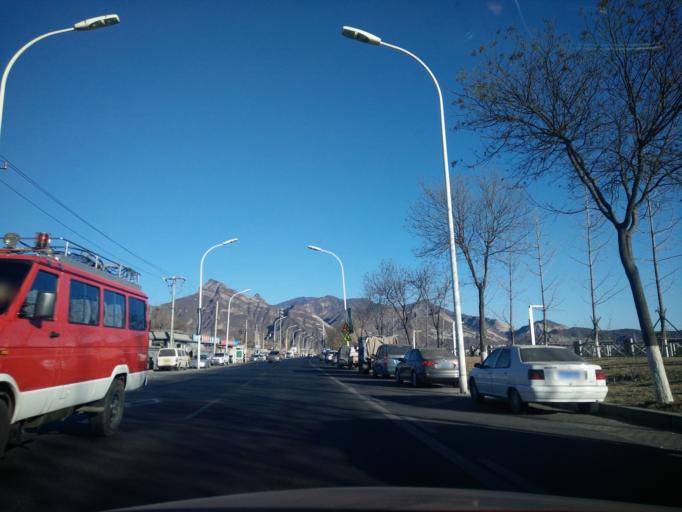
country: CN
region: Beijing
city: Junzhuang
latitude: 39.9813
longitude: 116.0823
